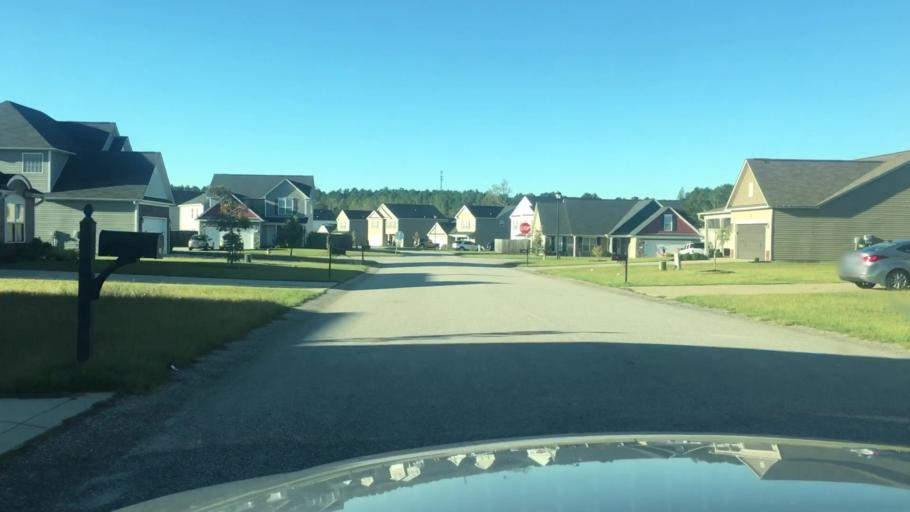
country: US
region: North Carolina
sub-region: Harnett County
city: Lillington
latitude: 35.3442
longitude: -78.8513
